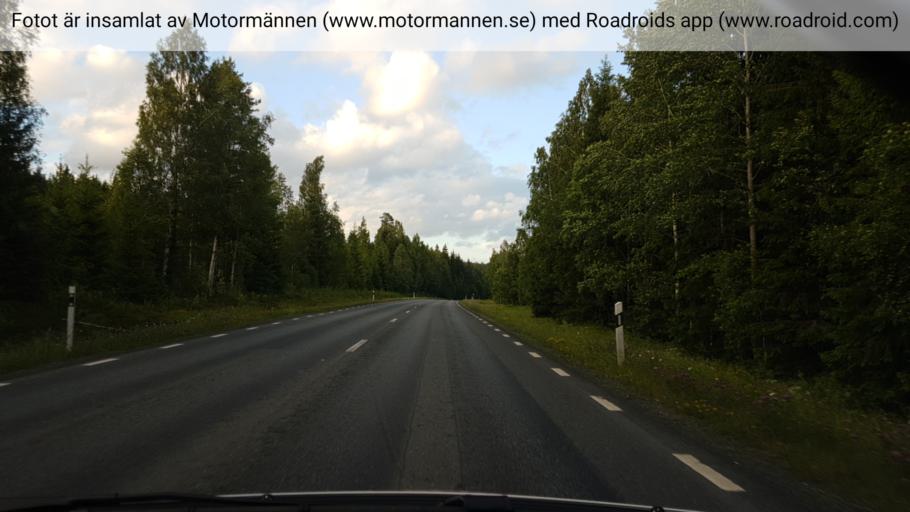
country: SE
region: OErebro
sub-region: Orebro Kommun
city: Garphyttan
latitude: 59.4449
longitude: 14.7815
